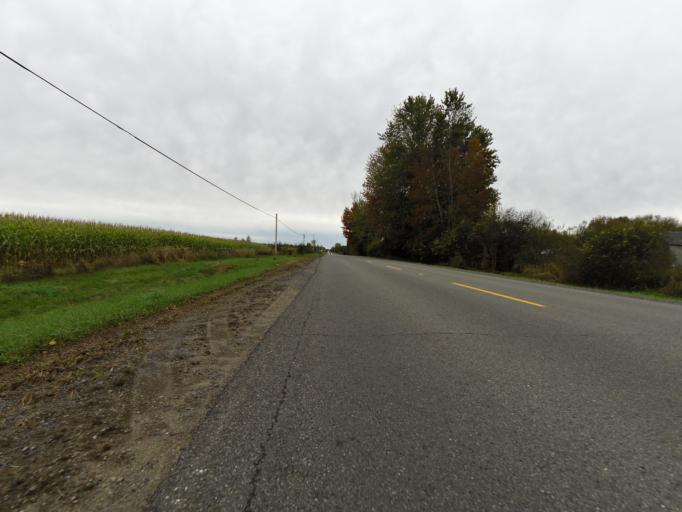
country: CA
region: Ontario
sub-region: Lanark County
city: Smiths Falls
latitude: 44.8539
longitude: -75.8121
